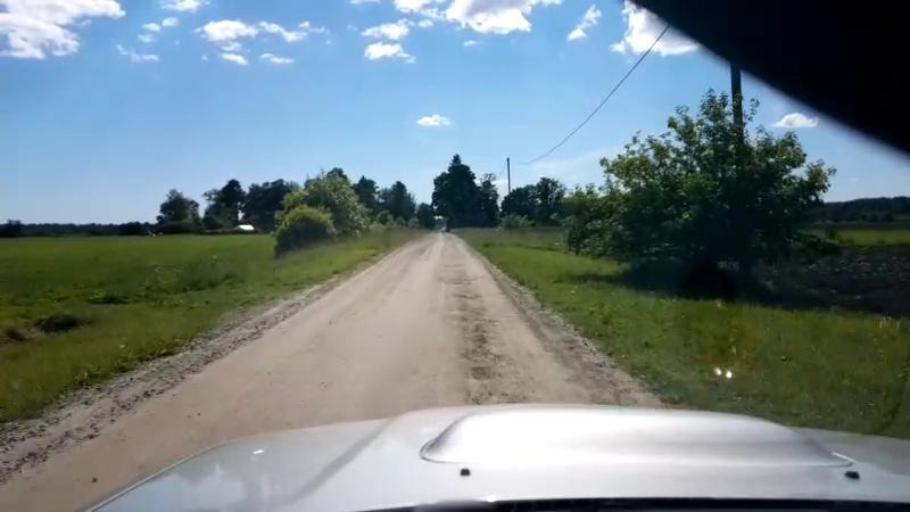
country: EE
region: Paernumaa
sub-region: Sauga vald
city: Sauga
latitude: 58.5160
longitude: 24.5171
